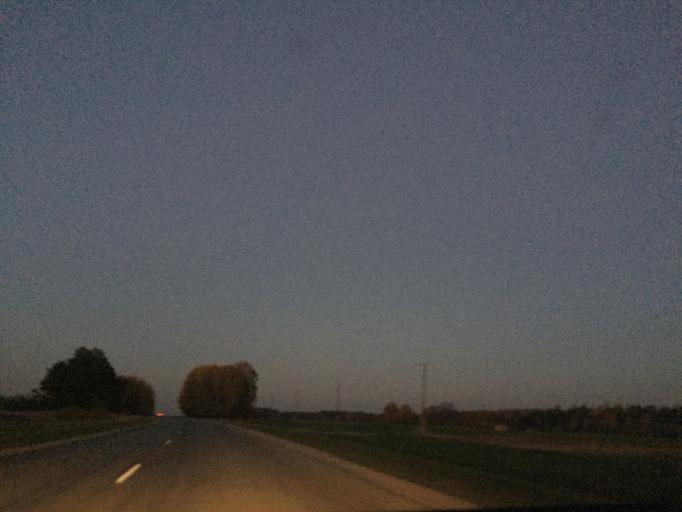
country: LV
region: Tervete
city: Zelmeni
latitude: 56.5119
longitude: 23.3027
